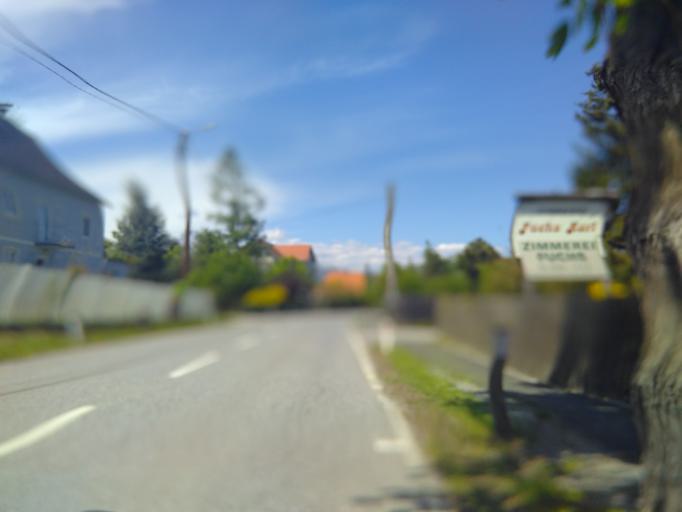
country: AT
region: Styria
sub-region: Politischer Bezirk Graz-Umgebung
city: Gratkorn
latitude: 47.1195
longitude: 15.3373
